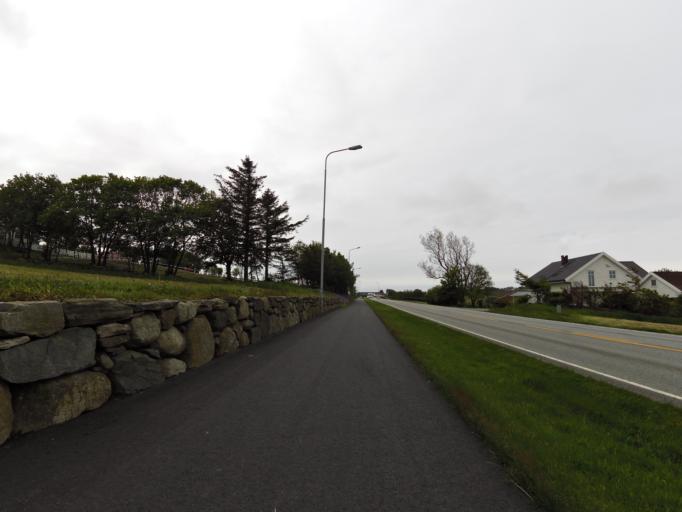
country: NO
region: Rogaland
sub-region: Klepp
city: Kleppe
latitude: 58.8305
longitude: 5.5955
